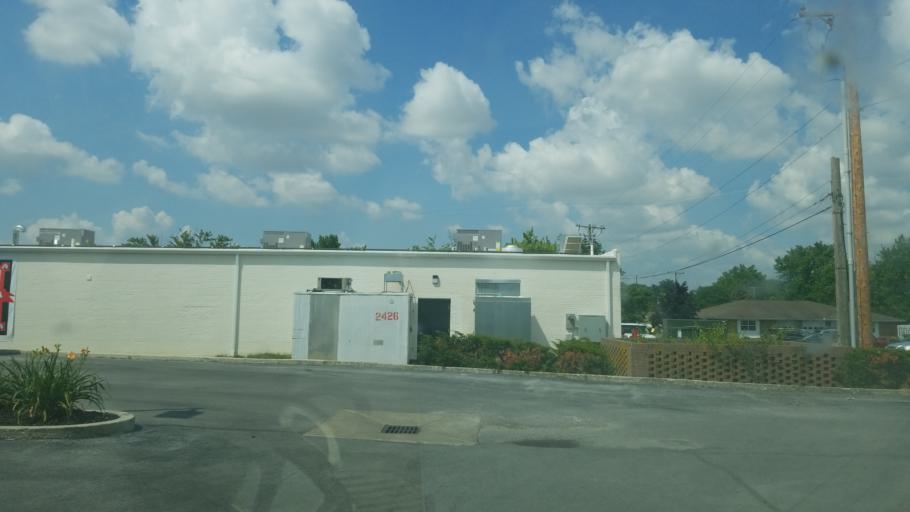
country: US
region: Ohio
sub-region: Auglaize County
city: Wapakoneta
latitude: 40.5796
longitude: -84.2035
